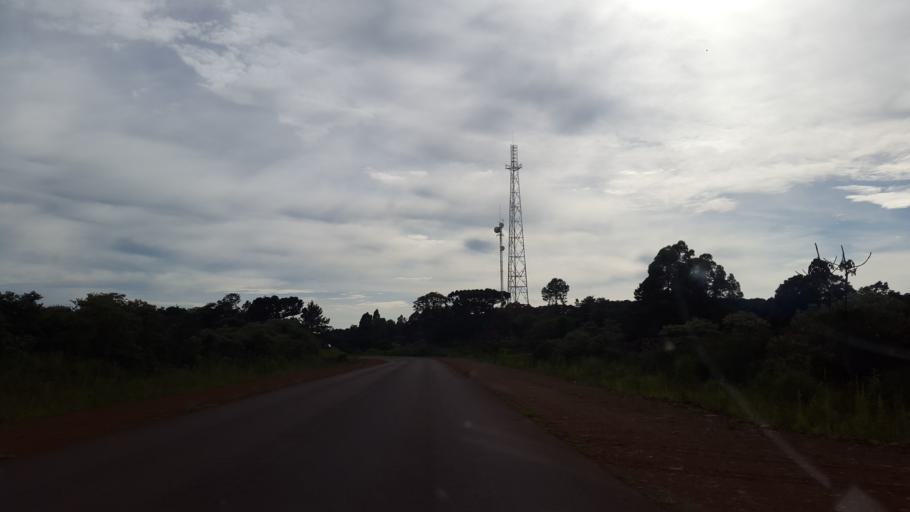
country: AR
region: Misiones
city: Bernardo de Irigoyen
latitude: -26.4264
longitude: -53.8446
